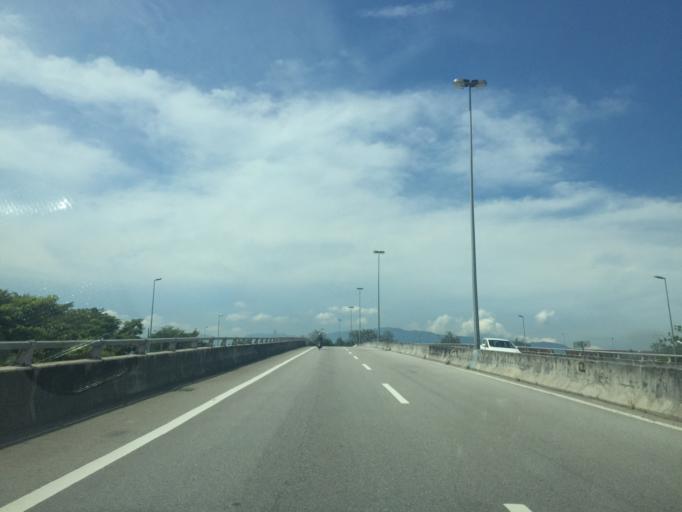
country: MY
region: Penang
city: Permatang Kuching
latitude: 5.4430
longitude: 100.3834
